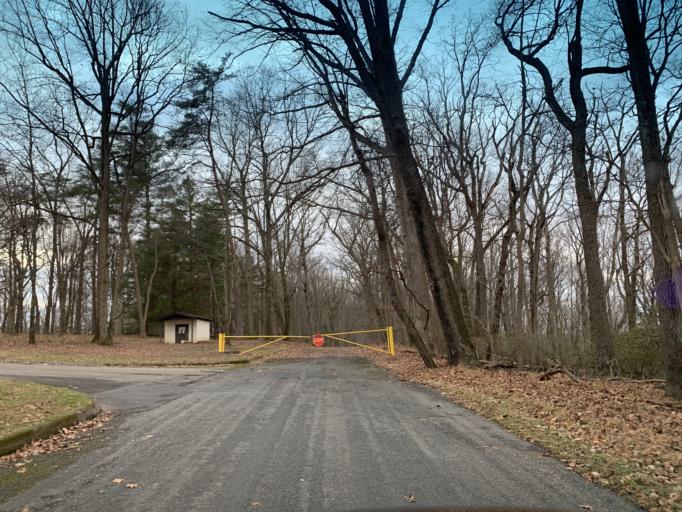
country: US
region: Maryland
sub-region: Harford County
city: Jarrettsville
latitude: 39.6354
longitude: -76.4170
